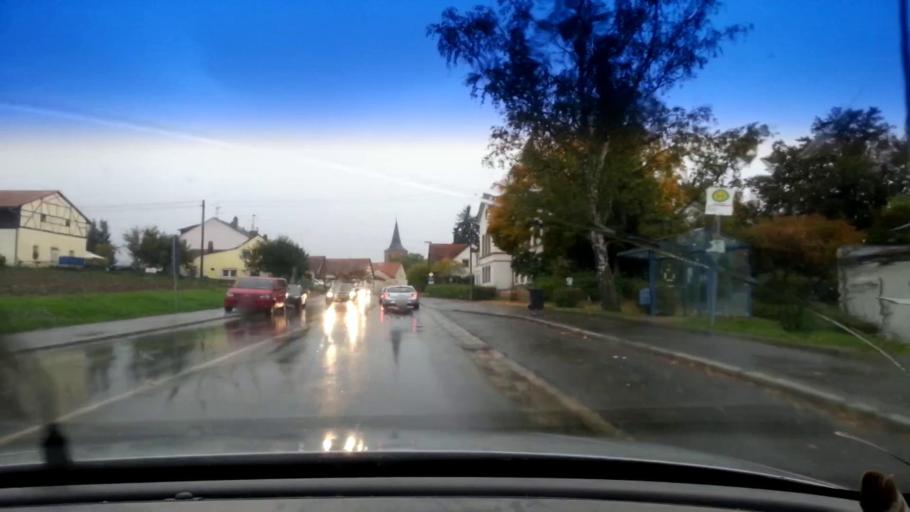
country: DE
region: Bavaria
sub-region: Upper Franconia
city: Schesslitz
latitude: 49.9787
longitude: 11.0386
